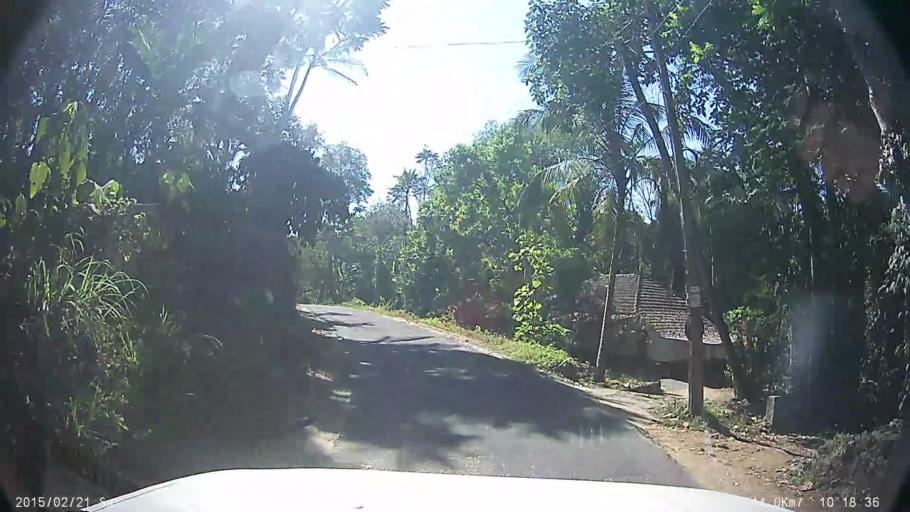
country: IN
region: Kerala
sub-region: Ernakulam
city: Muvattupuzha
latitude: 9.8748
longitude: 76.6532
